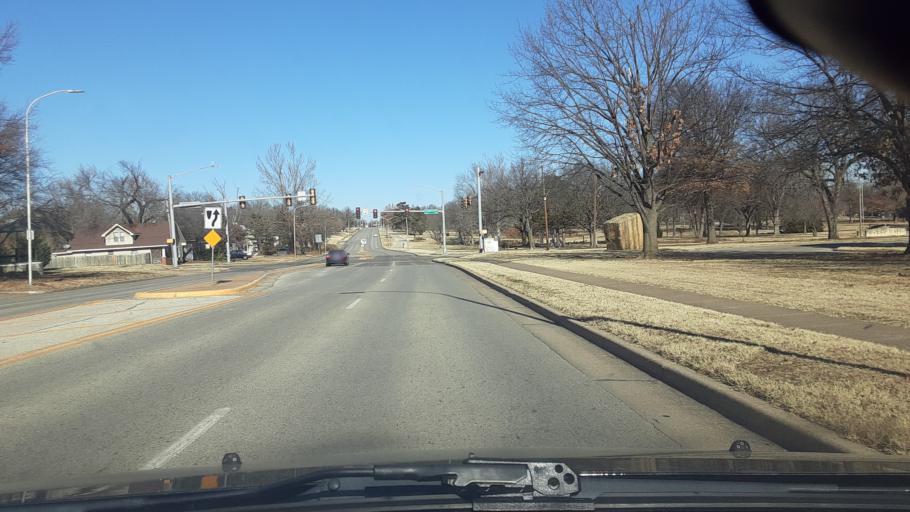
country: US
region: Oklahoma
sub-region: Kay County
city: Ponca City
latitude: 36.7089
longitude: -97.0783
